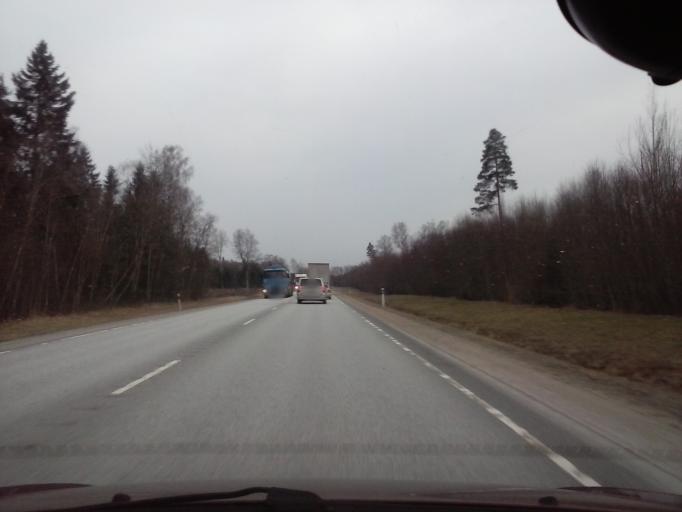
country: EE
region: Jaervamaa
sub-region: Paide linn
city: Paide
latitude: 58.9689
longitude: 25.6040
